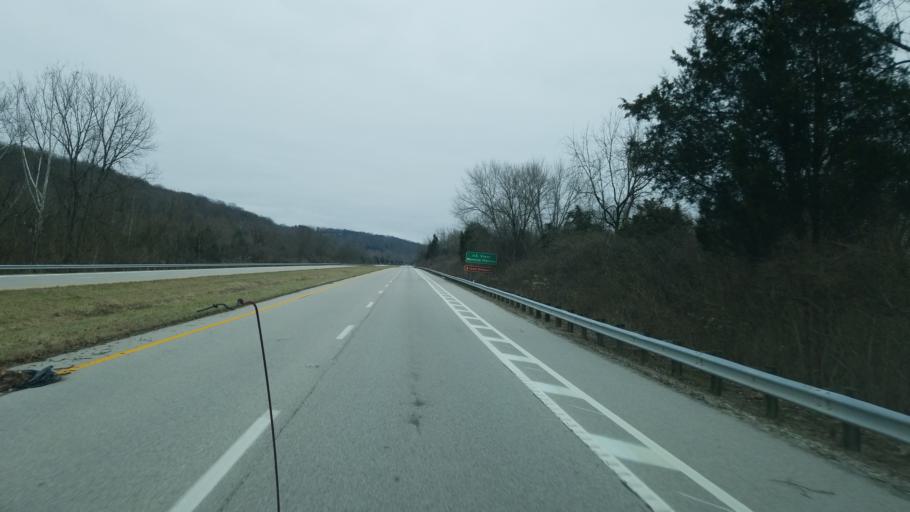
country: US
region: Ohio
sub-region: Hamilton County
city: Cherry Grove
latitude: 39.0315
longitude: -84.3291
